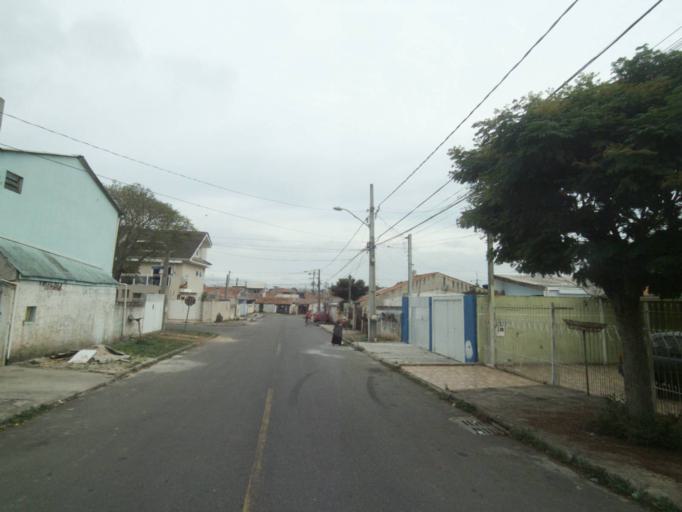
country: BR
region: Parana
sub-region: Sao Jose Dos Pinhais
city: Sao Jose dos Pinhais
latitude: -25.5527
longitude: -49.2676
